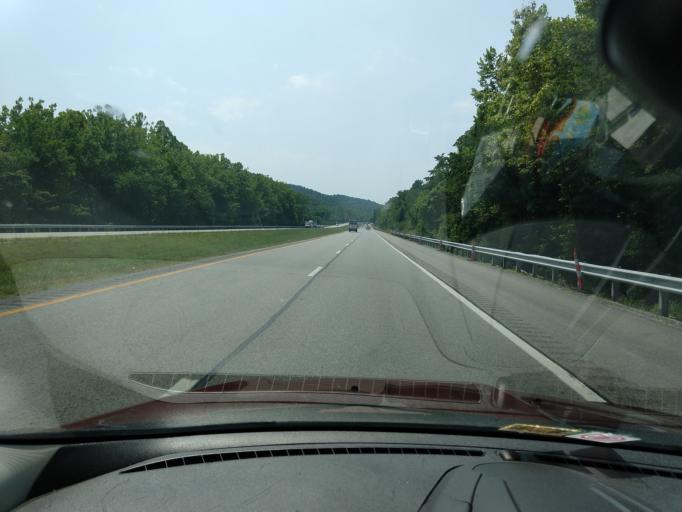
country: US
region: West Virginia
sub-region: Jackson County
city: Ripley
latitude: 38.7116
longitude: -81.6442
